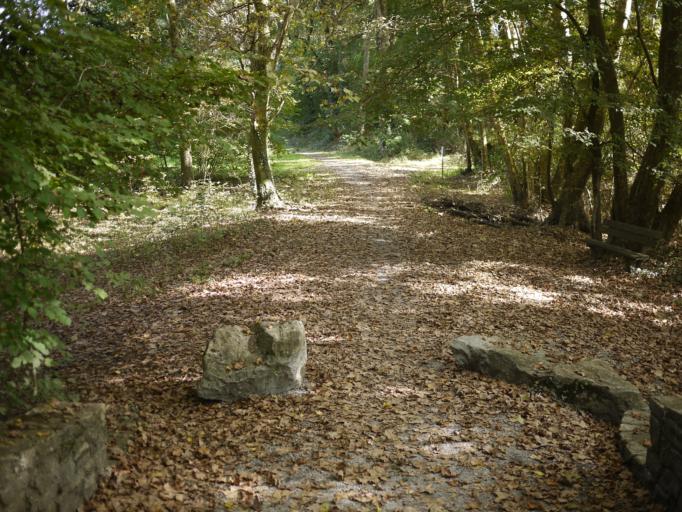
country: FR
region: Aquitaine
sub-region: Departement des Landes
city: Saint-Paul-les-Dax
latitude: 43.7240
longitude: -1.0688
